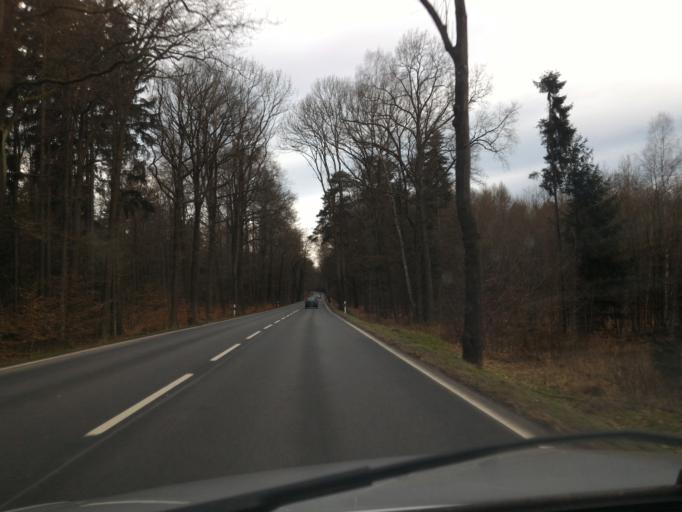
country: DE
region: Saxony
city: Arnsdorf
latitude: 51.0643
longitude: 13.9668
